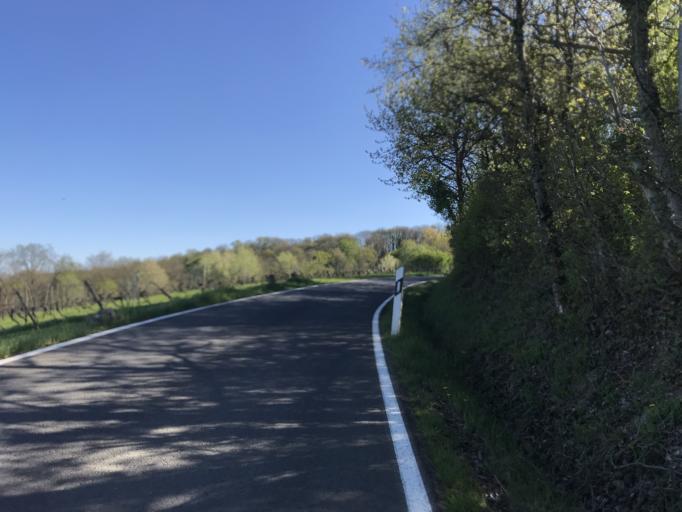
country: DE
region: Rheinland-Pfalz
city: Ingelheim am Rhein
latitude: 49.9457
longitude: 8.0556
